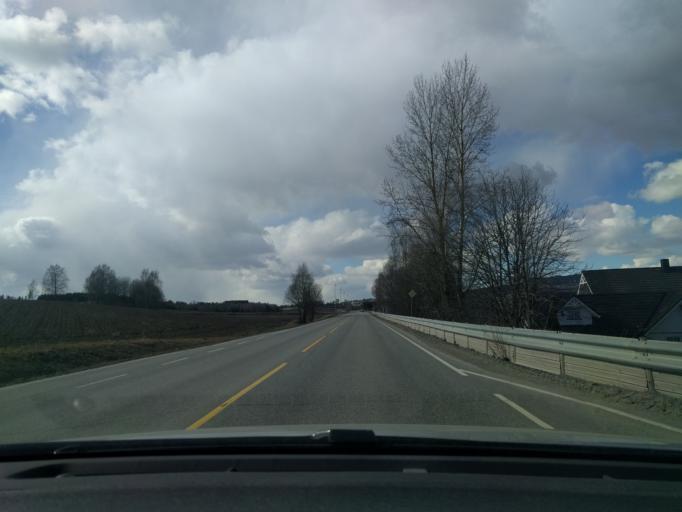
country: NO
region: Hedmark
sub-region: Hamar
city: Hamar
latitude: 60.8364
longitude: 11.0549
